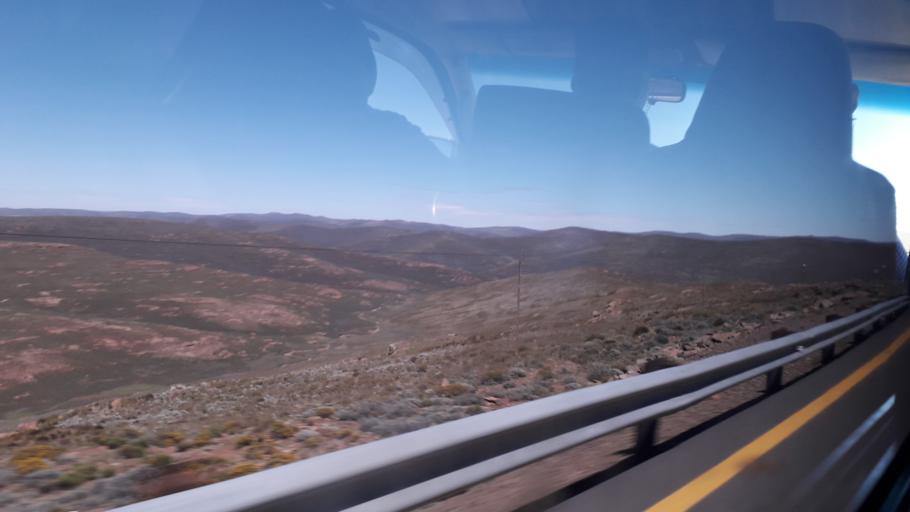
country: LS
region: Mokhotlong
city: Mokhotlong
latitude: -29.0184
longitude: 28.8503
